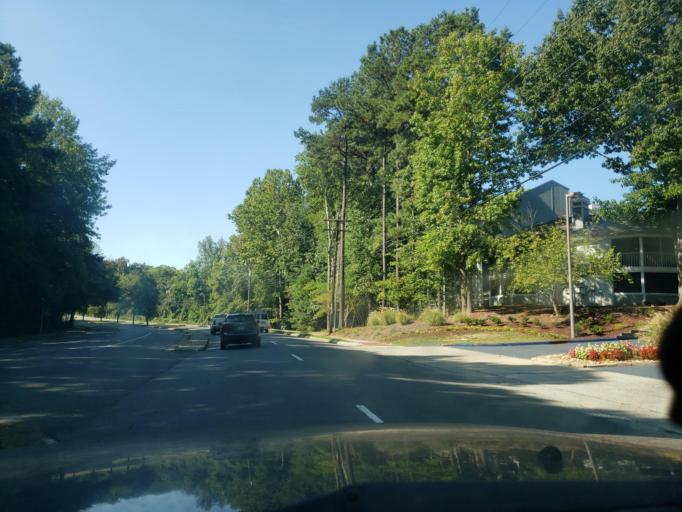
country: US
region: North Carolina
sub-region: Durham County
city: Durham
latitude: 35.9589
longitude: -78.9657
